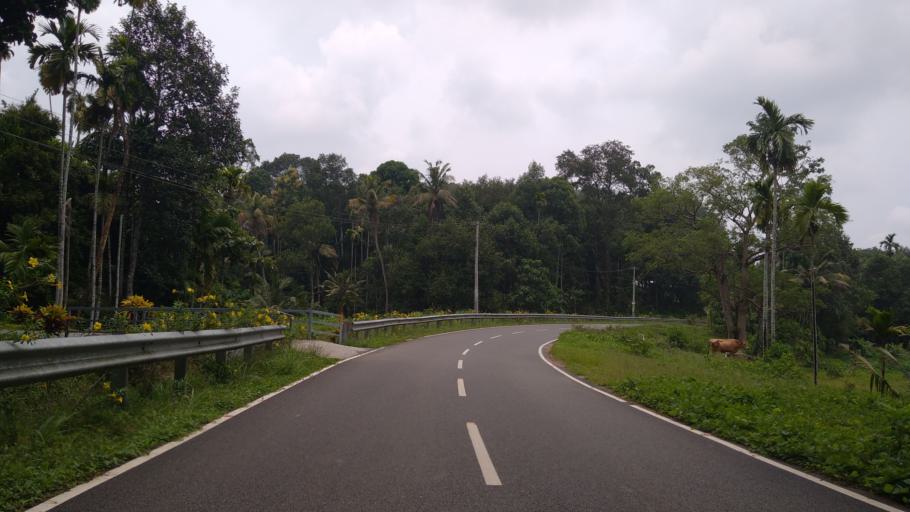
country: IN
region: Kerala
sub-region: Ernakulam
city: Ramamangalam
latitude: 10.0156
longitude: 76.4856
